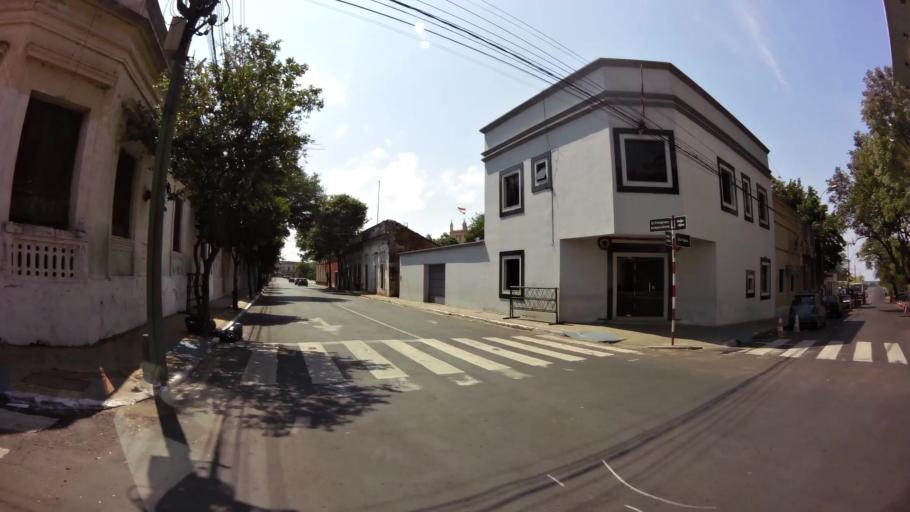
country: PY
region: Asuncion
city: Asuncion
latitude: -25.2790
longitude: -57.6365
